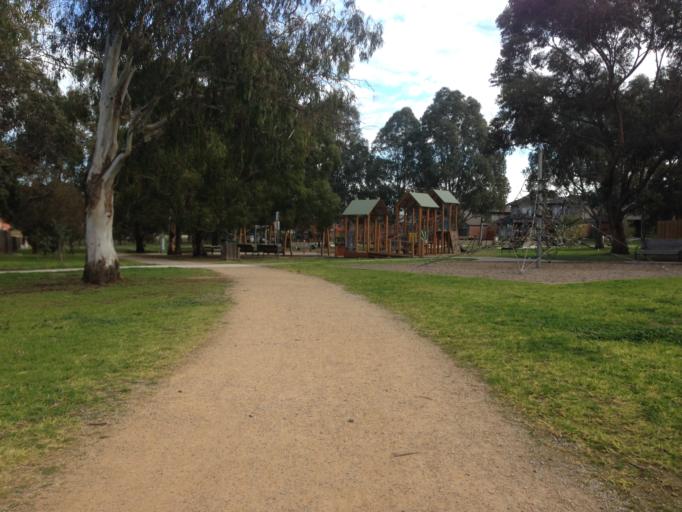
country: AU
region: Victoria
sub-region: Banyule
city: Bellfield
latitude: -37.7607
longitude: 145.0397
